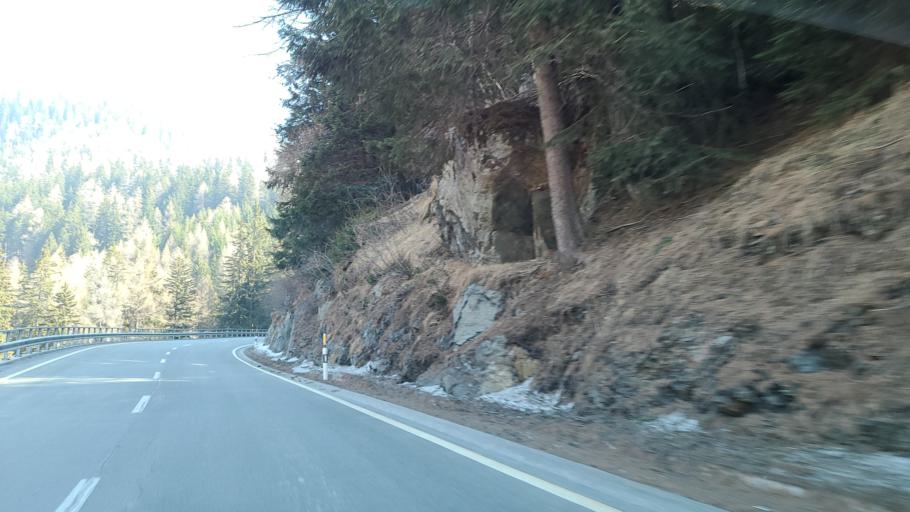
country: CH
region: Grisons
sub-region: Bernina District
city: Poschiavo
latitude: 46.3842
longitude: 10.0775
